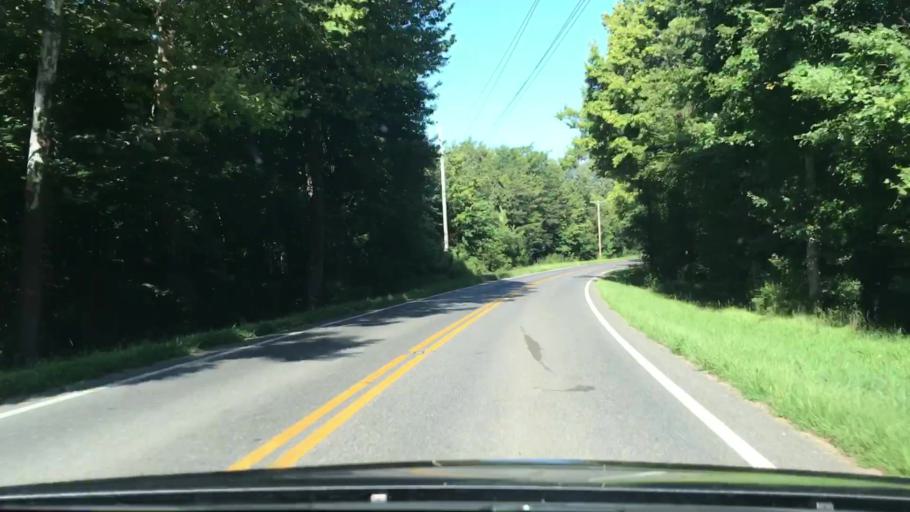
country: US
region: Kentucky
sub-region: Graves County
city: Mayfield
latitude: 36.7790
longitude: -88.5184
